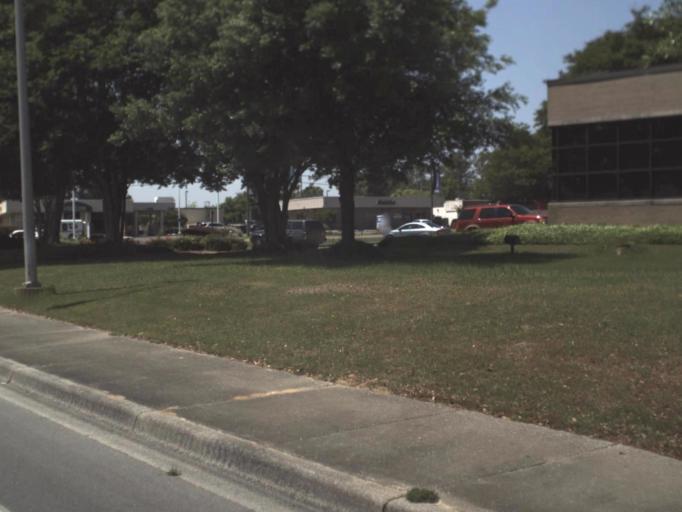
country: US
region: Florida
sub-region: Escambia County
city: Ferry Pass
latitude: 30.4781
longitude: -87.1974
